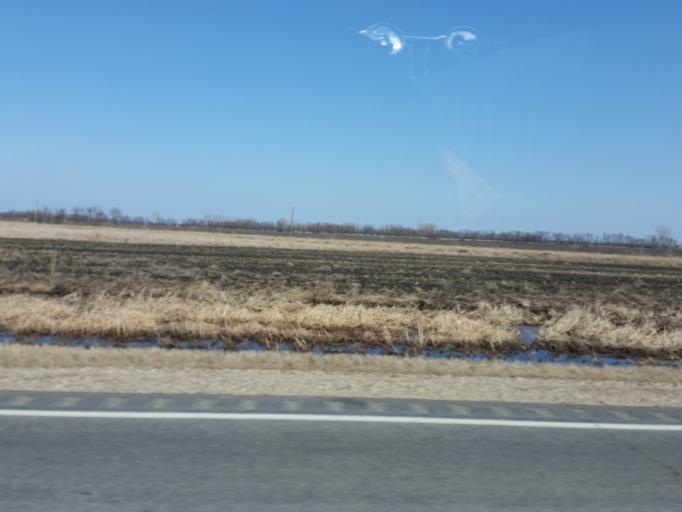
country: US
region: North Dakota
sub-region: Grand Forks County
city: Grand Forks Air Force Base
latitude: 48.1247
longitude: -97.2358
